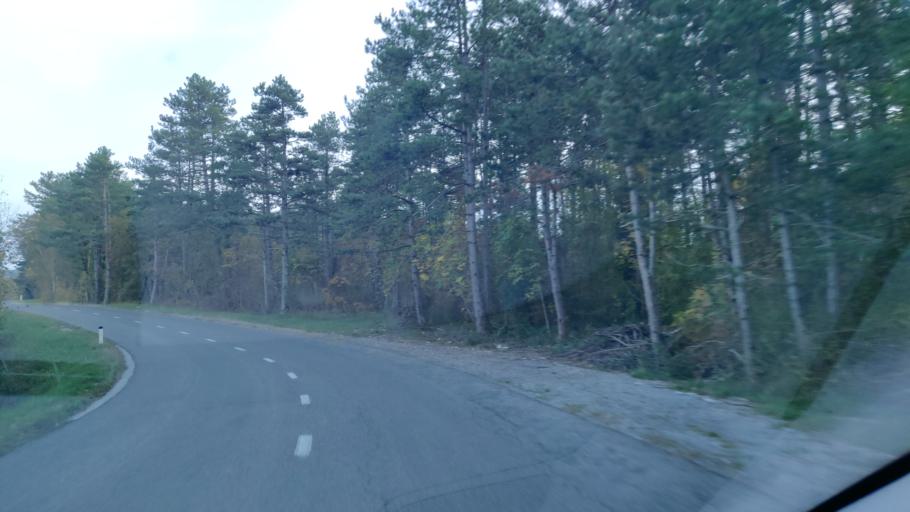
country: IT
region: Friuli Venezia Giulia
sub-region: Provincia di Trieste
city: Zolla
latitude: 45.8033
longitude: 13.8476
